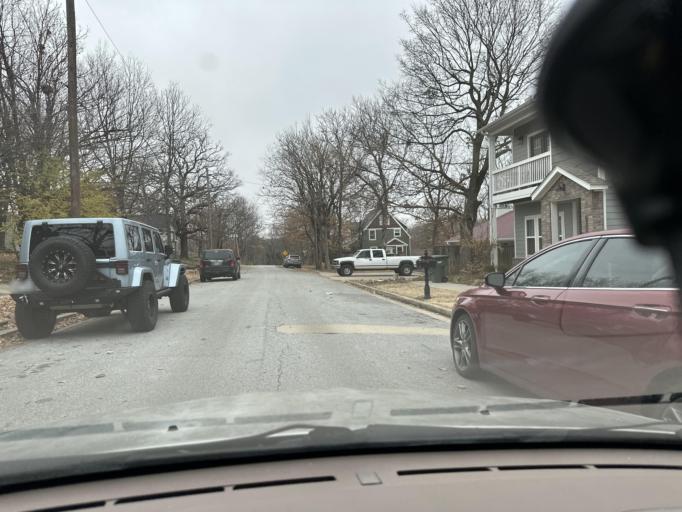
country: US
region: Arkansas
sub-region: Washington County
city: Fayetteville
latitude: 36.0705
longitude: -94.1591
